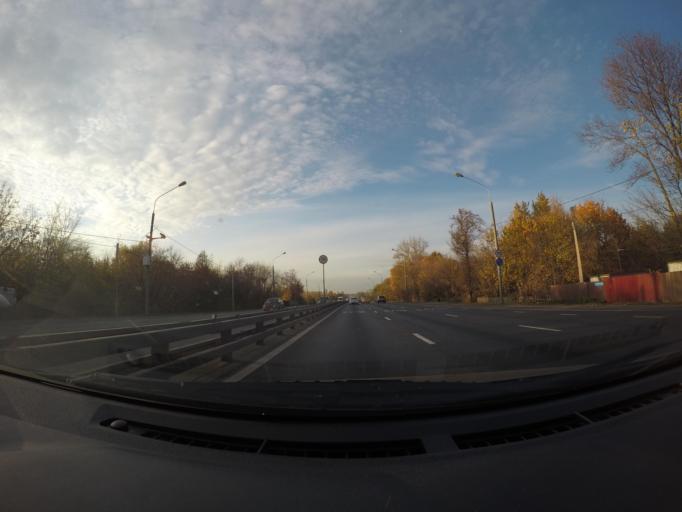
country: RU
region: Moskovskaya
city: Novopodrezkovo
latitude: 55.9262
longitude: 37.3850
